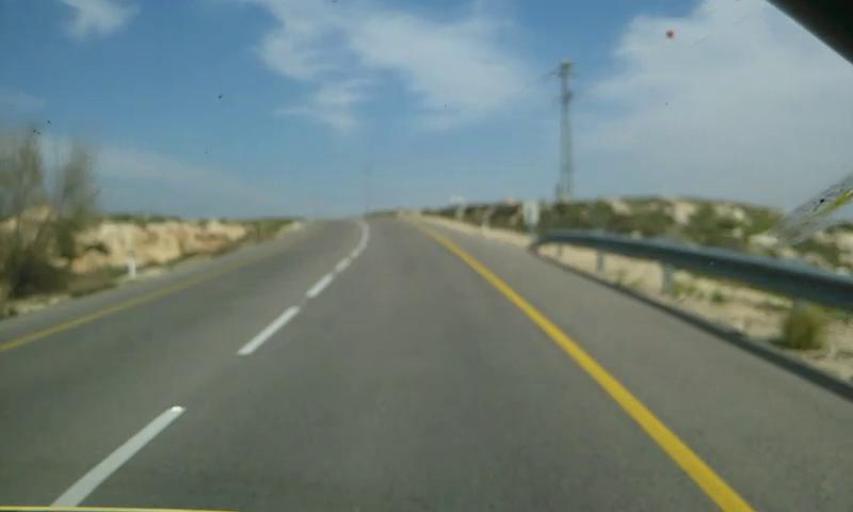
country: PS
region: West Bank
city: As Samu`
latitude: 31.3945
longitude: 35.0238
